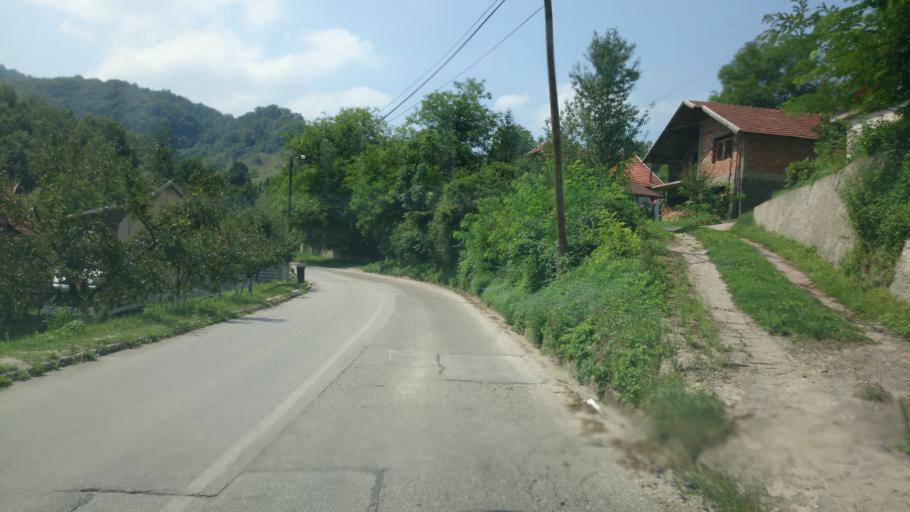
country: BA
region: Federation of Bosnia and Herzegovina
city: Lokvine
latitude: 44.1900
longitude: 17.8671
